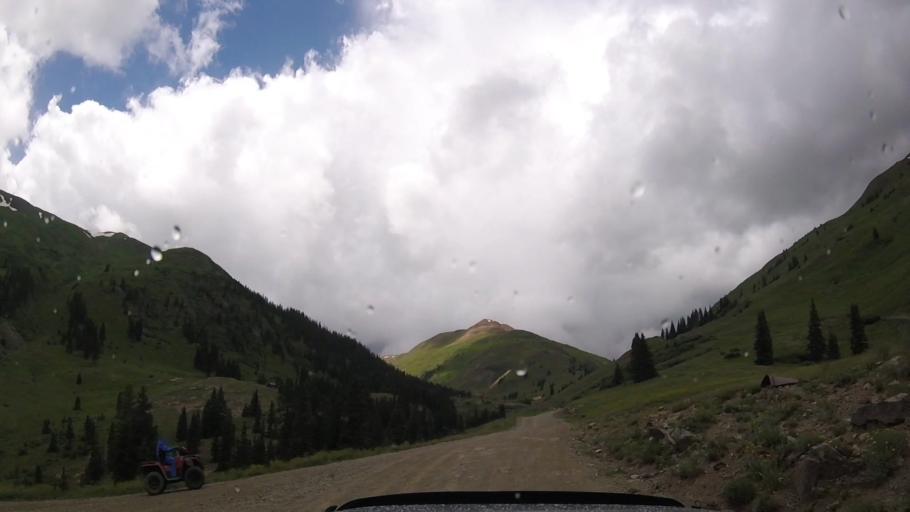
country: US
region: Colorado
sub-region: Ouray County
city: Ouray
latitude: 37.9269
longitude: -107.5637
